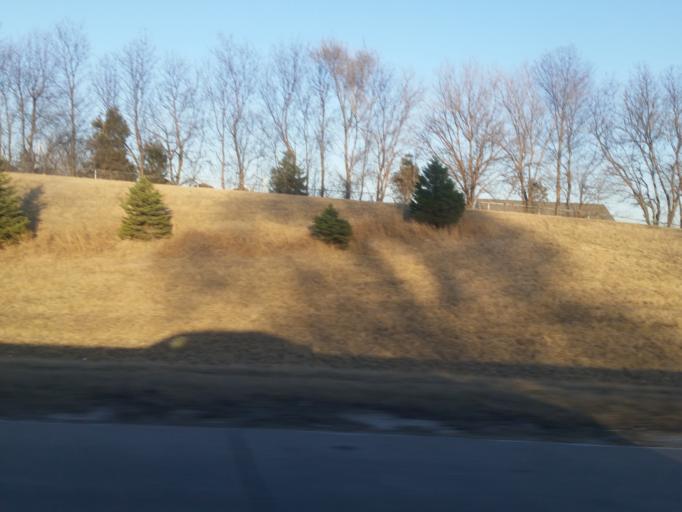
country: US
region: Nebraska
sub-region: Sarpy County
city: Offutt Air Force Base
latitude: 41.1745
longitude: -95.9397
